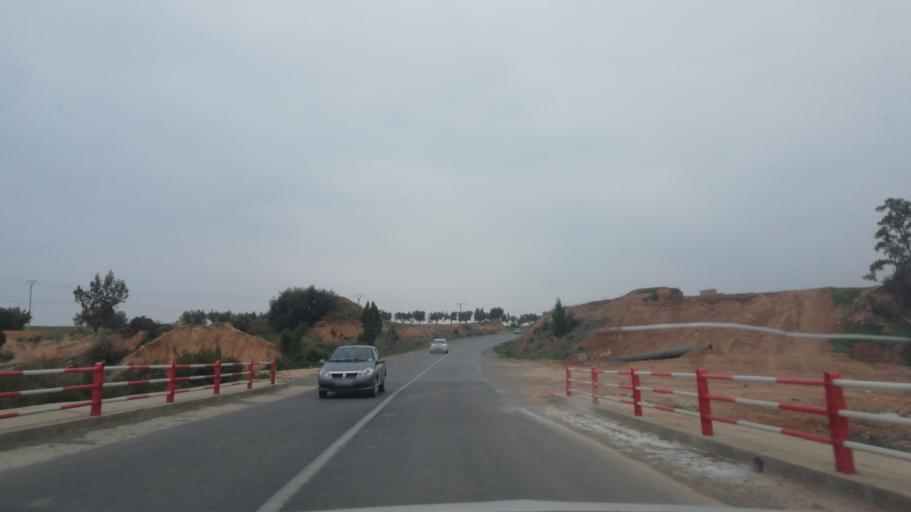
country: DZ
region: Sidi Bel Abbes
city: Sfizef
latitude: 35.2738
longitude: -0.1555
